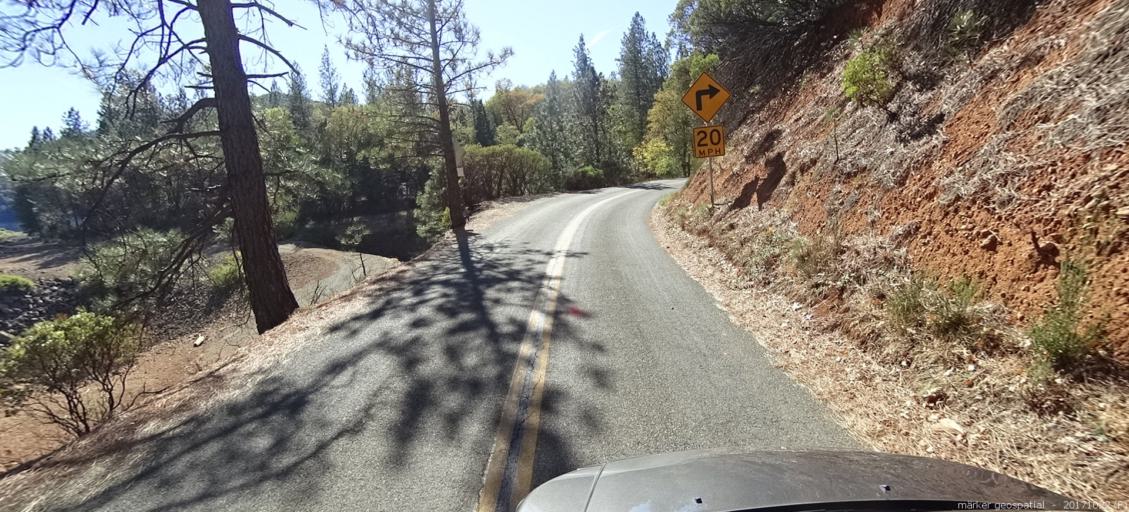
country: US
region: California
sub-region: Shasta County
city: Central Valley (historical)
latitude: 40.8620
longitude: -122.3967
